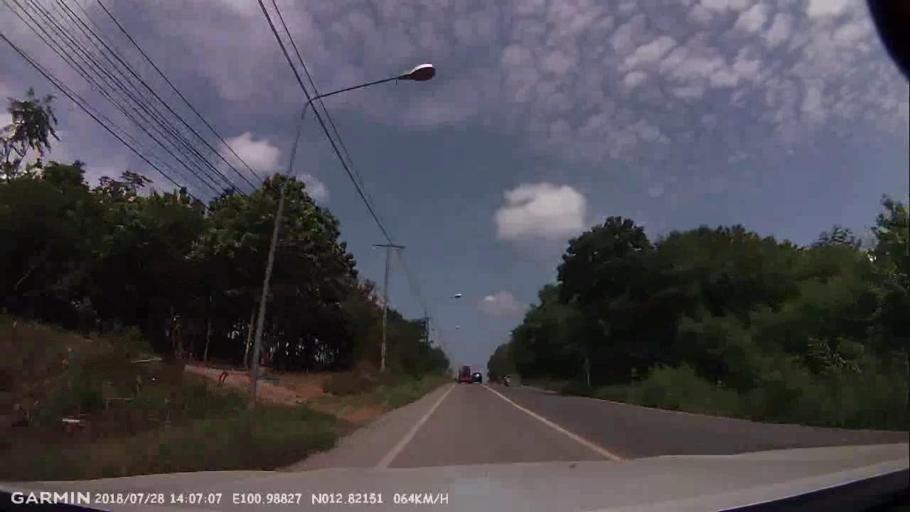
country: TH
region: Rayong
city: Ban Chang
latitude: 12.8214
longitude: 100.9884
